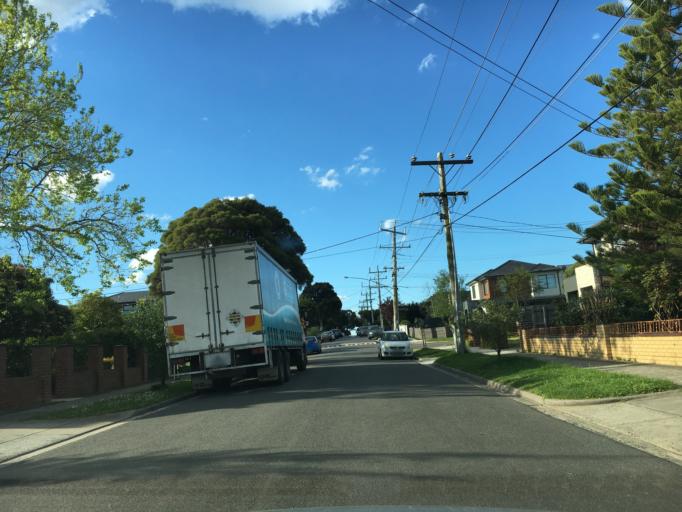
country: AU
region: Victoria
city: Clayton
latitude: -37.9046
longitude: 145.1136
